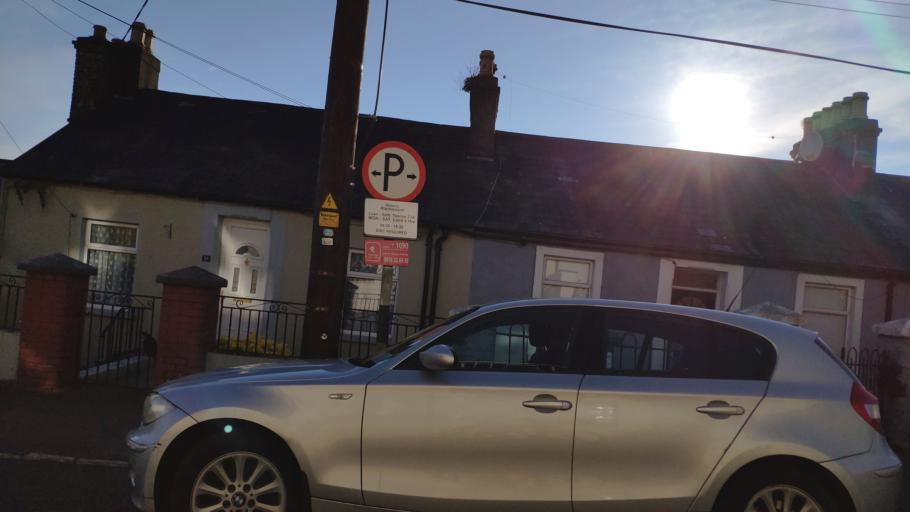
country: IE
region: Munster
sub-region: County Cork
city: Cork
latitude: 51.9042
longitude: -8.4713
